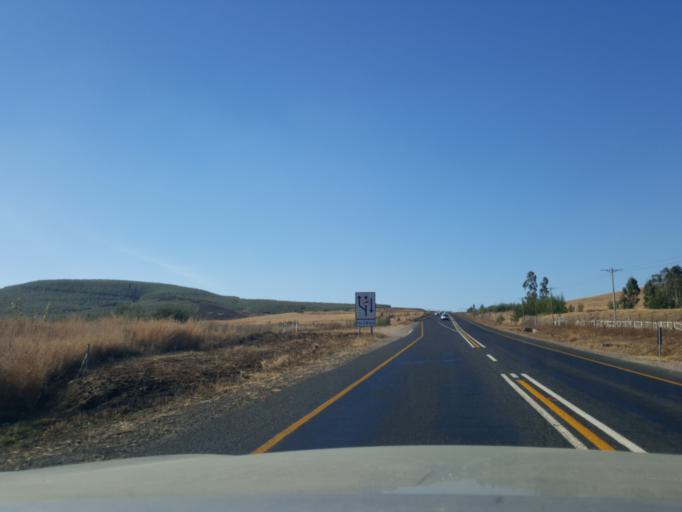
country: ZA
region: Mpumalanga
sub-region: Nkangala District Municipality
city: Belfast
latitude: -25.6044
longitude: 30.2842
